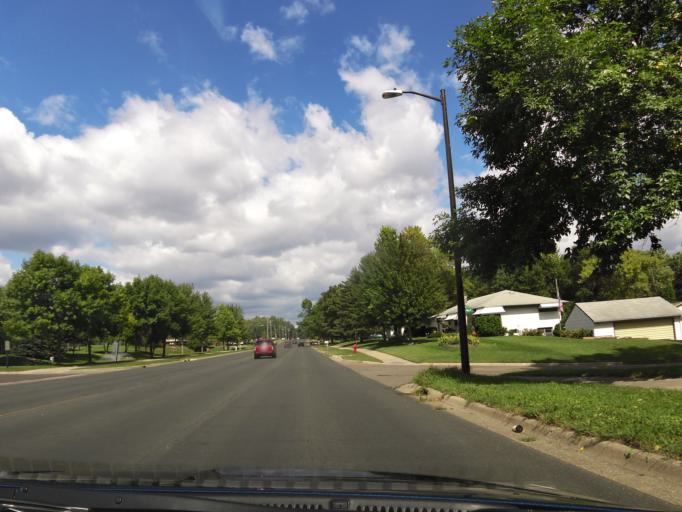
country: US
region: Minnesota
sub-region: Dakota County
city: Inver Grove Heights
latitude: 44.8570
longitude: -93.0449
